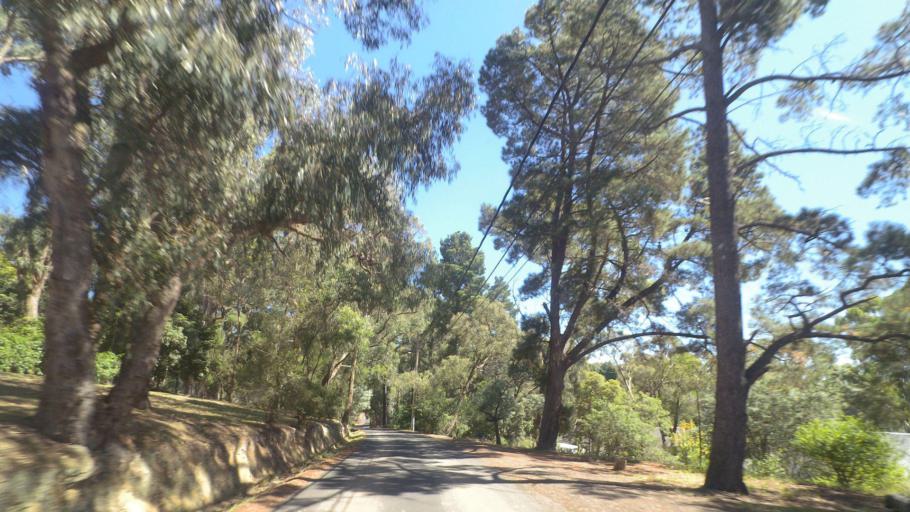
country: AU
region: Victoria
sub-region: Manningham
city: Donvale
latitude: -37.7888
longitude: 145.1888
